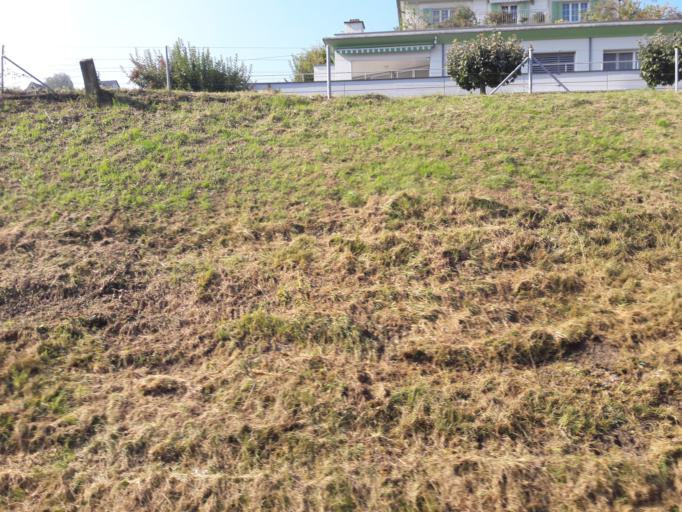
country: CH
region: Schwyz
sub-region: Bezirk Kuessnacht
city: Kussnacht
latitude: 47.0833
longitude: 8.4327
